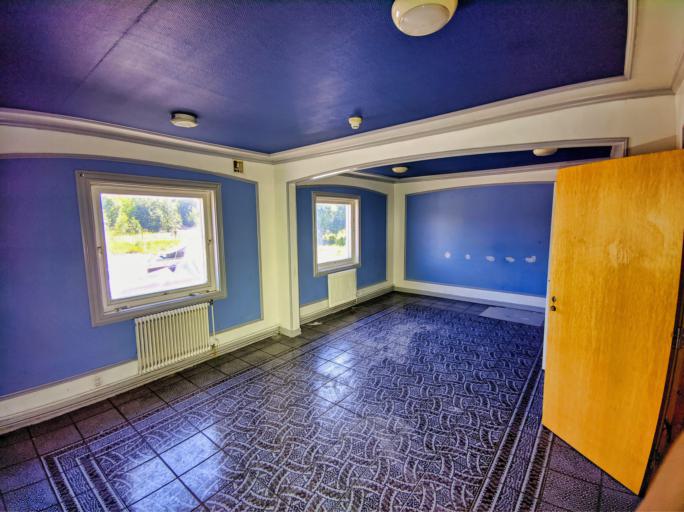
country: NO
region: Akershus
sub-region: Nes
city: Neskollen
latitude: 60.1329
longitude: 11.2844
